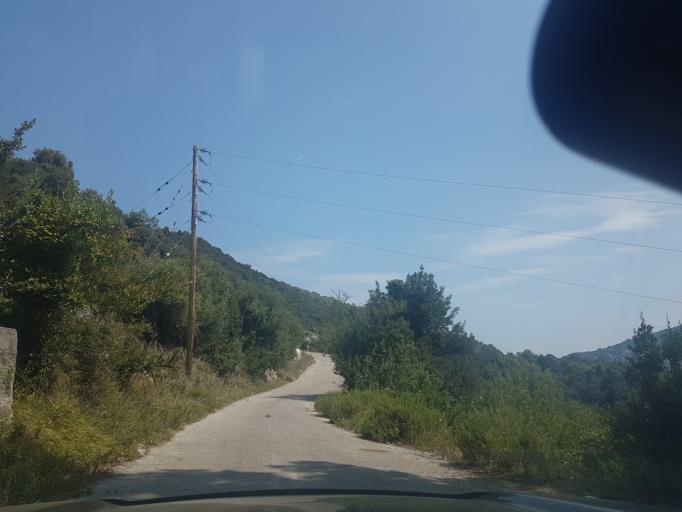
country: GR
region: Central Greece
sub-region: Nomos Evvoias
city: Yimnon
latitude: 38.6223
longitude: 23.8876
